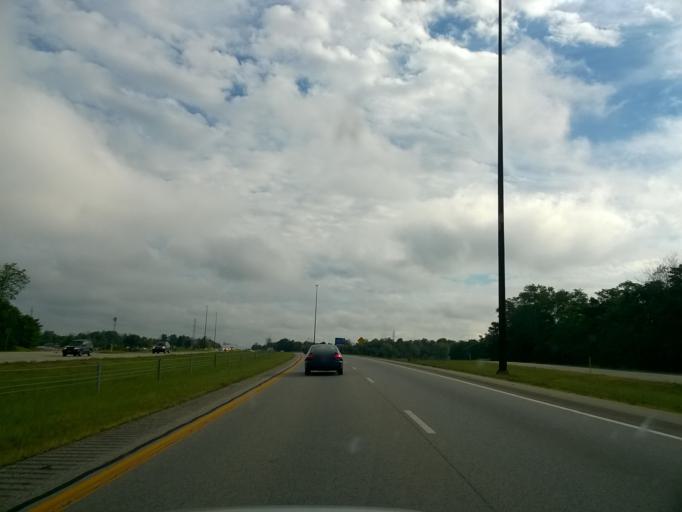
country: US
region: Indiana
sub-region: Floyd County
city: Georgetown
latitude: 38.2857
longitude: -85.9136
